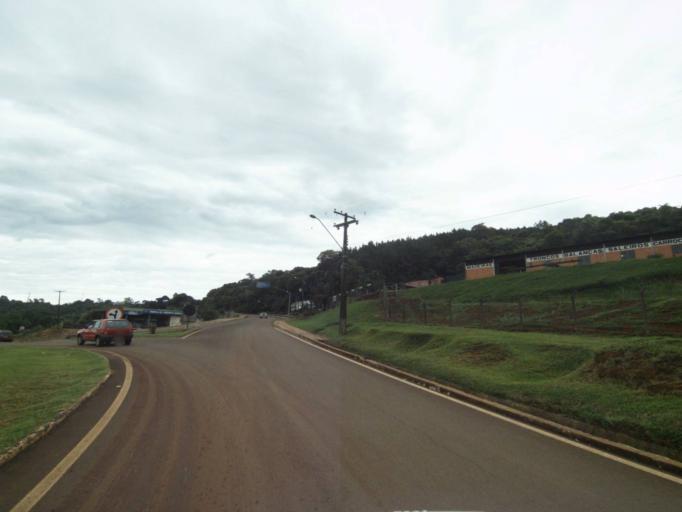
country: BR
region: Parana
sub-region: Guaraniacu
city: Guaraniacu
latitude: -25.1089
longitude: -52.8555
